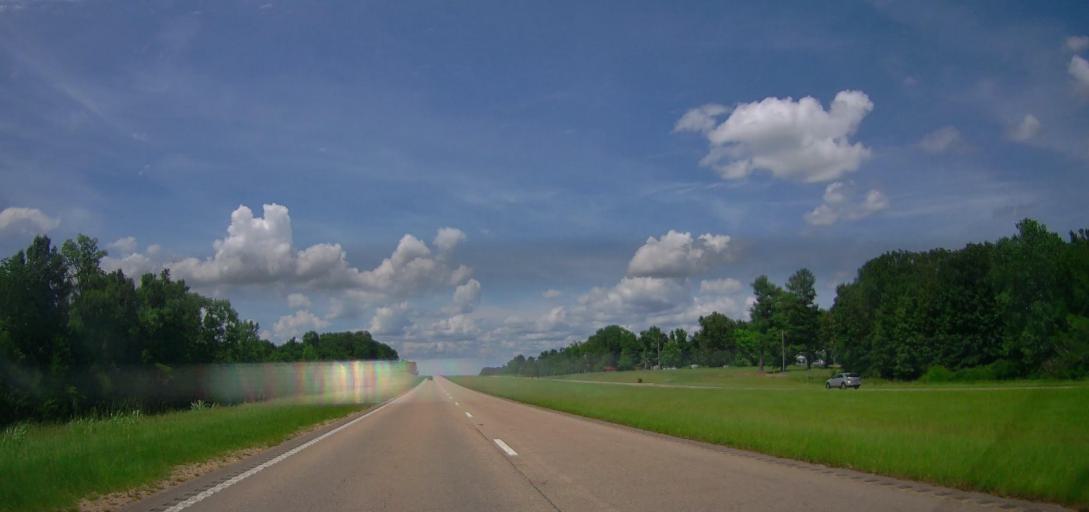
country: US
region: Mississippi
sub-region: Lee County
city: Nettleton
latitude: 34.0270
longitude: -88.6325
